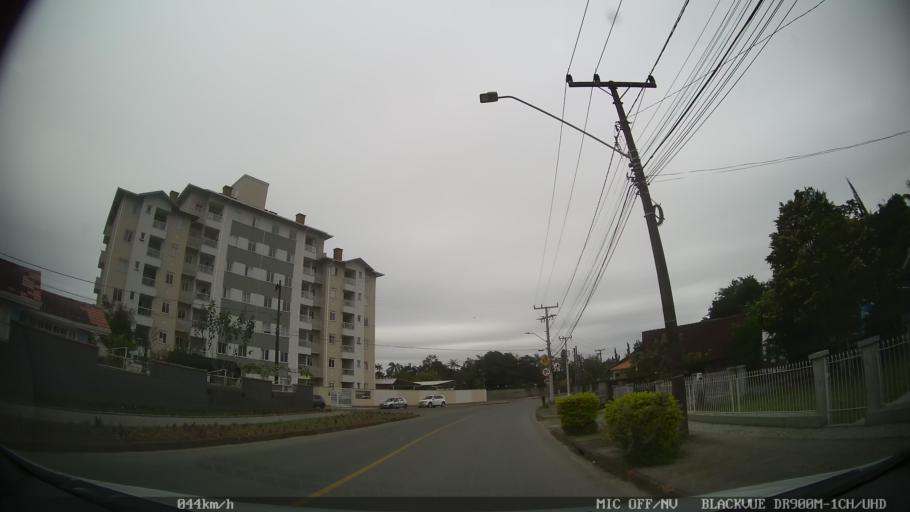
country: BR
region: Santa Catarina
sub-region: Joinville
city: Joinville
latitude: -26.1992
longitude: -48.9084
